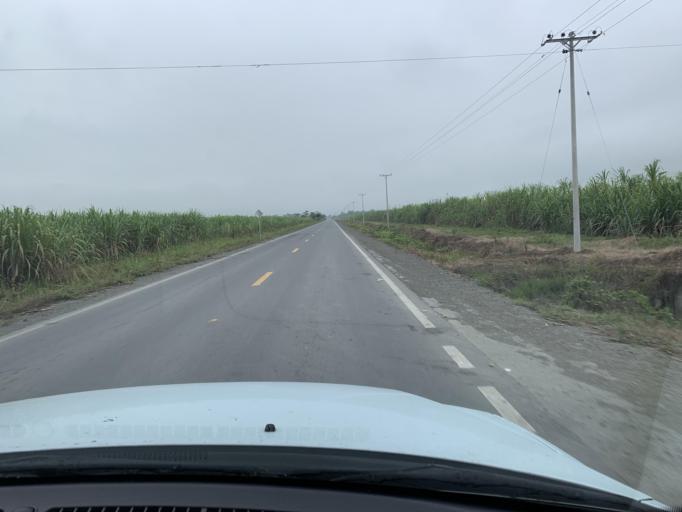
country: EC
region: Guayas
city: Coronel Marcelino Mariduena
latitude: -2.3231
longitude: -79.5202
